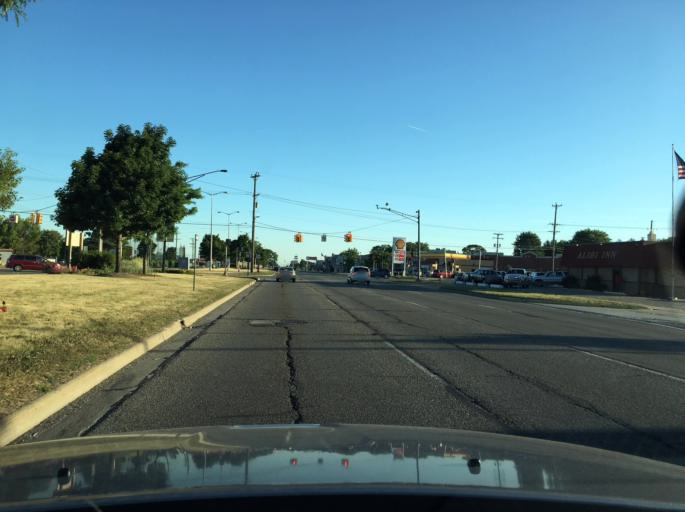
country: US
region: Michigan
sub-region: Macomb County
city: Fraser
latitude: 42.5405
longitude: -82.9087
